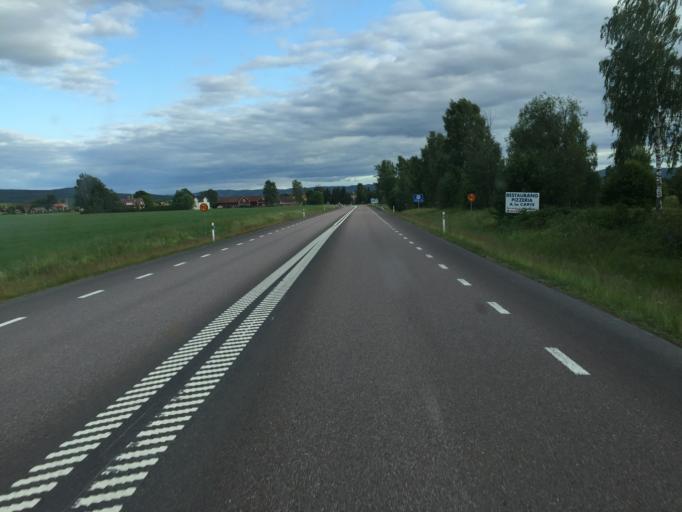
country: SE
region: Dalarna
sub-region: Gagnefs Kommun
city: Gagnef
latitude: 60.5939
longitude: 15.0821
